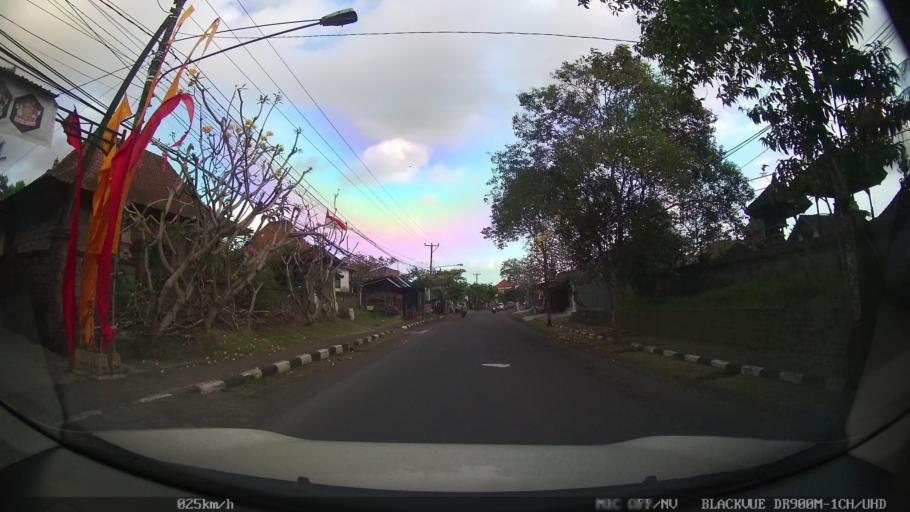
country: ID
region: Bali
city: Banjar Mambalkajanan
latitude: -8.5629
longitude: 115.2207
